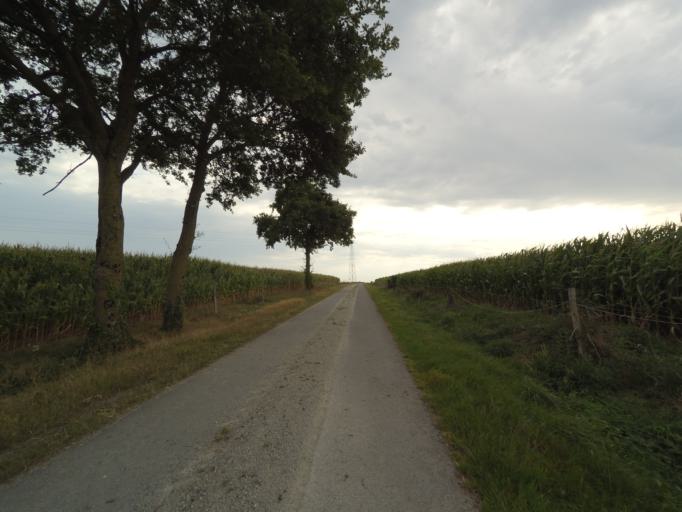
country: FR
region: Pays de la Loire
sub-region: Departement de la Vendee
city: Bouffere
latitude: 46.9806
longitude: -1.3614
